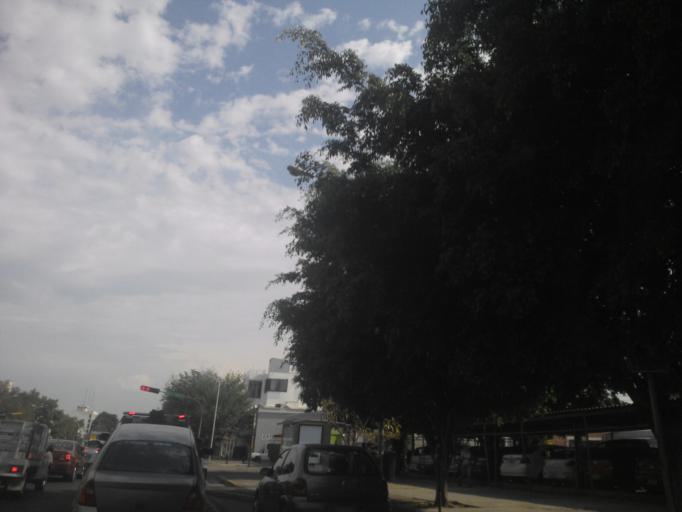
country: MX
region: Jalisco
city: Guadalajara
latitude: 20.6739
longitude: -103.3548
